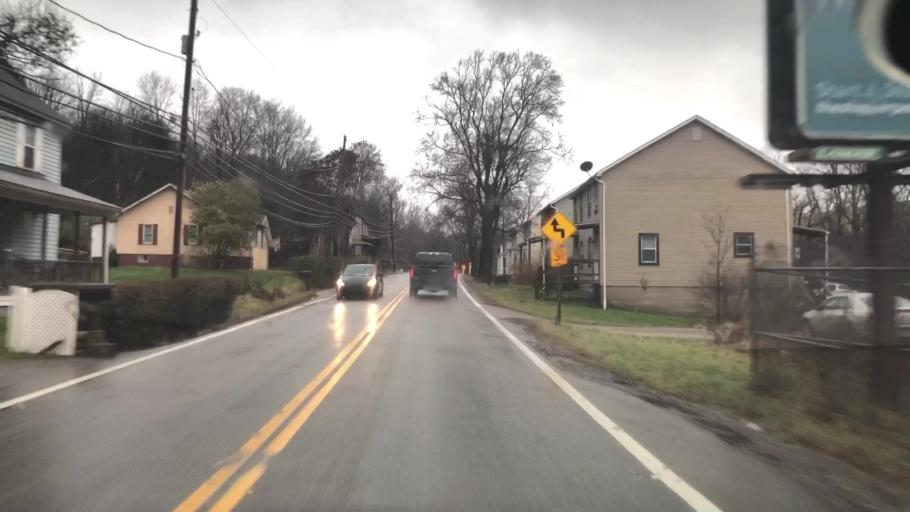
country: US
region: Ohio
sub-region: Belmont County
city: Saint Clairsville
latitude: 40.0930
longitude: -80.9097
